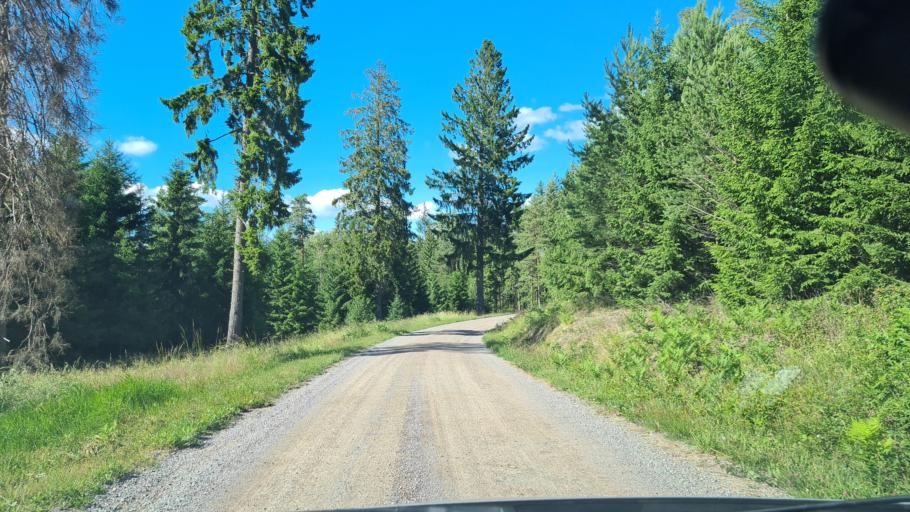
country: SE
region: OEstergoetland
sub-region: Norrkopings Kommun
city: Krokek
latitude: 58.6945
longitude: 16.4256
